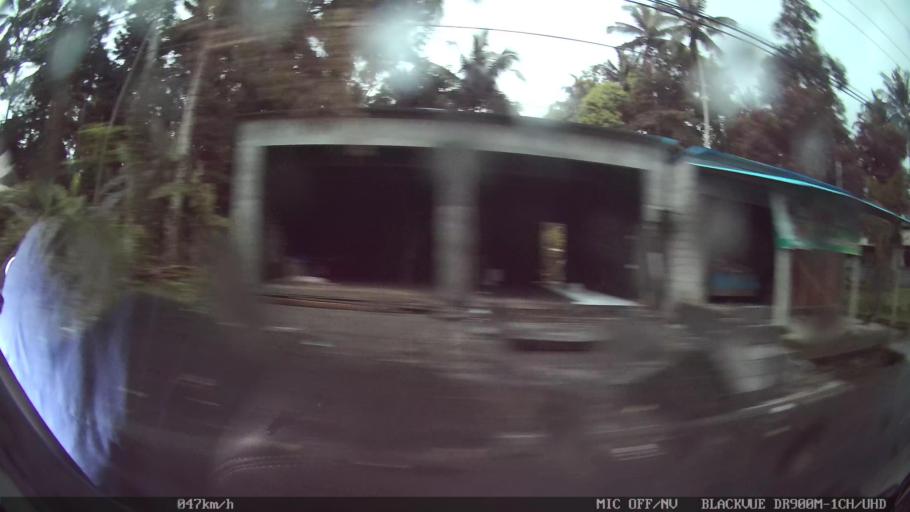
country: ID
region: Bali
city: Banjar Tengah
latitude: -8.5020
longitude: 115.1884
